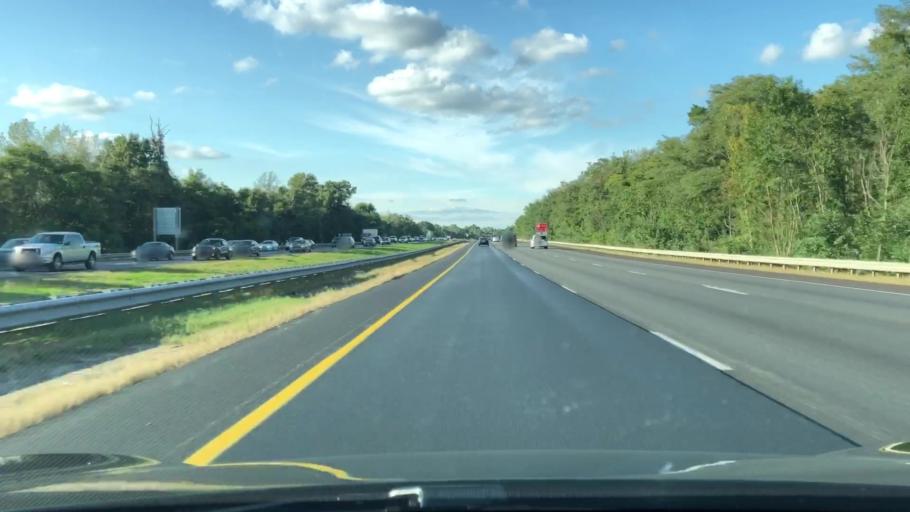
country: US
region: New Jersey
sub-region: Burlington County
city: Bordentown
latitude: 40.1644
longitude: -74.7200
